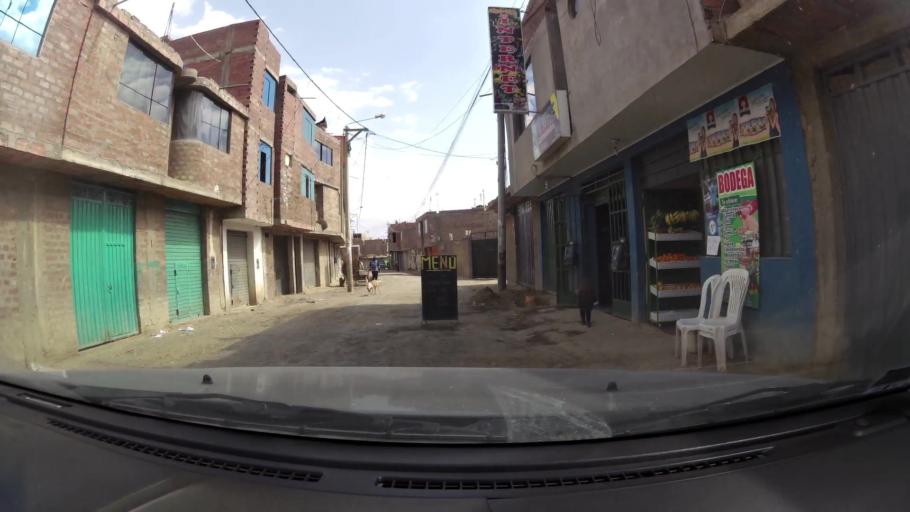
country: PE
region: Junin
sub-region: Provincia de Huancayo
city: Huancayo
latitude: -12.0945
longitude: -75.1989
